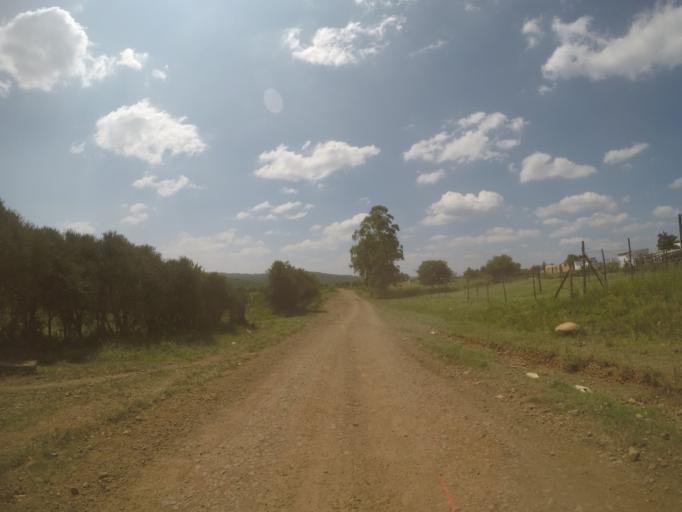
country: ZA
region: KwaZulu-Natal
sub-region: uThungulu District Municipality
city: Empangeni
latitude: -28.5902
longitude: 31.7366
